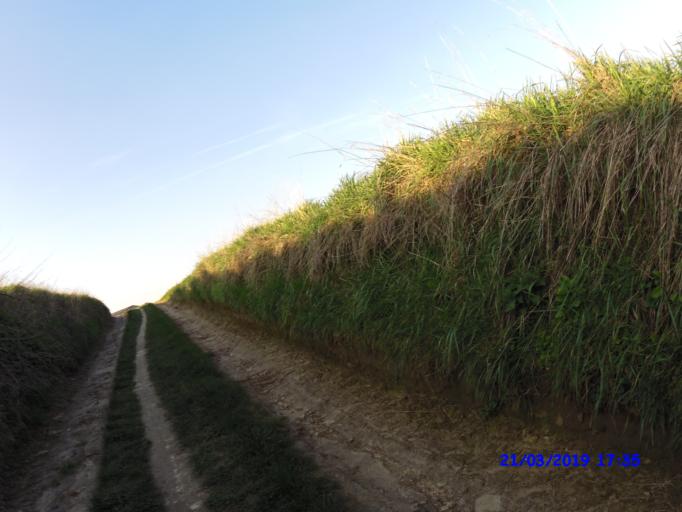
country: BE
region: Flanders
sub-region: Provincie Vlaams-Brabant
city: Sint-Genesius-Rode
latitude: 50.7592
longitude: 4.3563
